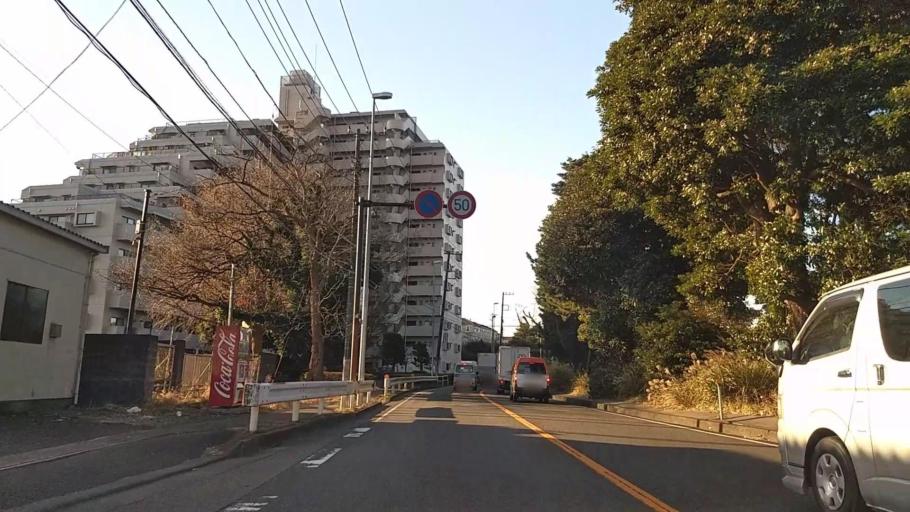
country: JP
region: Kanagawa
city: Fujisawa
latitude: 35.3831
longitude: 139.5146
